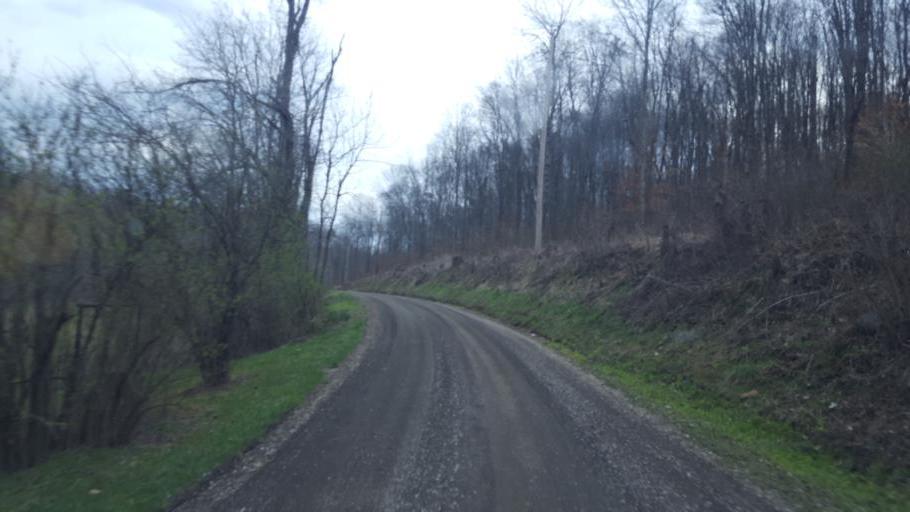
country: US
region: Ohio
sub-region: Guernsey County
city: Mantua
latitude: 40.1218
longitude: -81.8048
